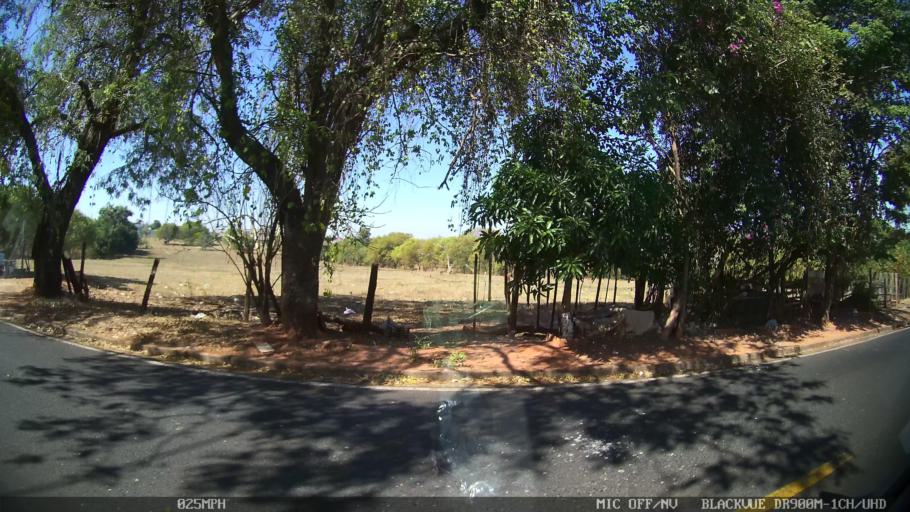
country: BR
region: Sao Paulo
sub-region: Sao Jose Do Rio Preto
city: Sao Jose do Rio Preto
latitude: -20.7722
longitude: -49.3996
